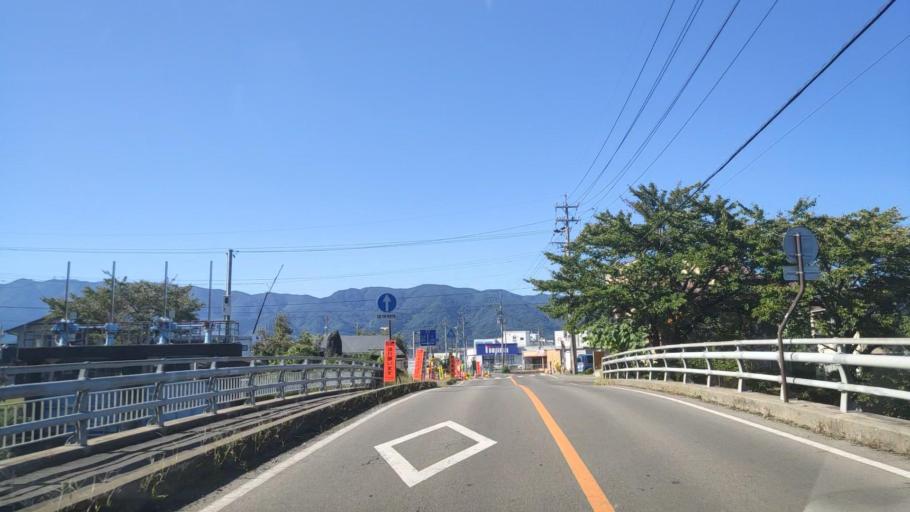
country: JP
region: Nagano
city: Suwa
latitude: 36.0363
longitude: 138.1115
